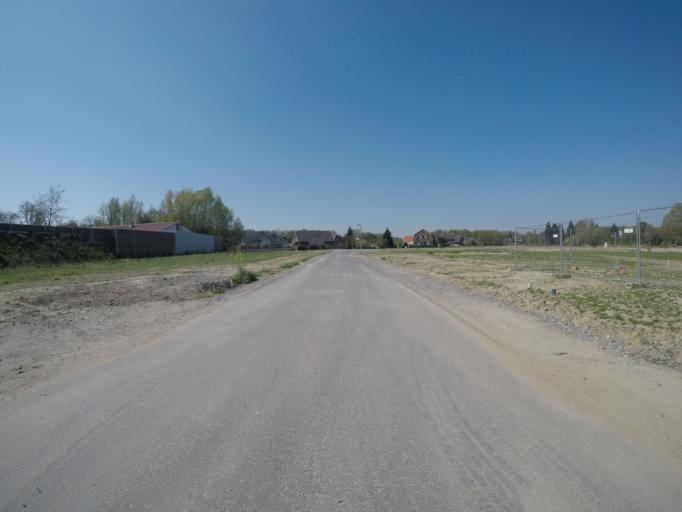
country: DE
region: North Rhine-Westphalia
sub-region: Regierungsbezirk Munster
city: Isselburg
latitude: 51.8471
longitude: 6.4372
